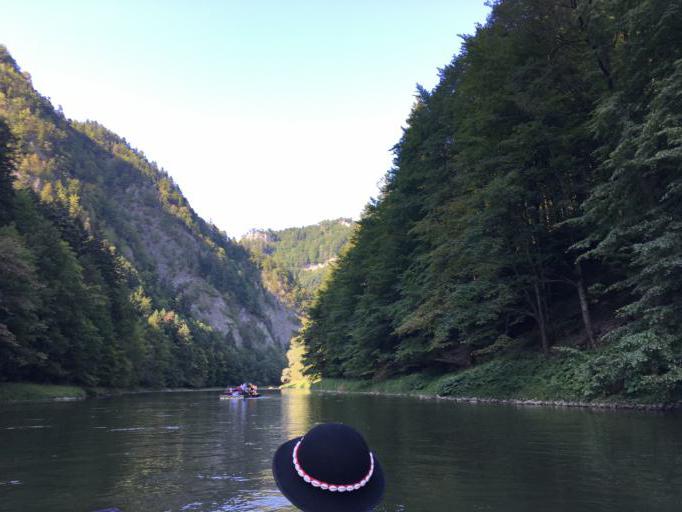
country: PL
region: Lesser Poland Voivodeship
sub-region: Powiat nowotarski
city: Kroscienko nad Dunajcem
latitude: 49.4125
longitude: 20.4293
